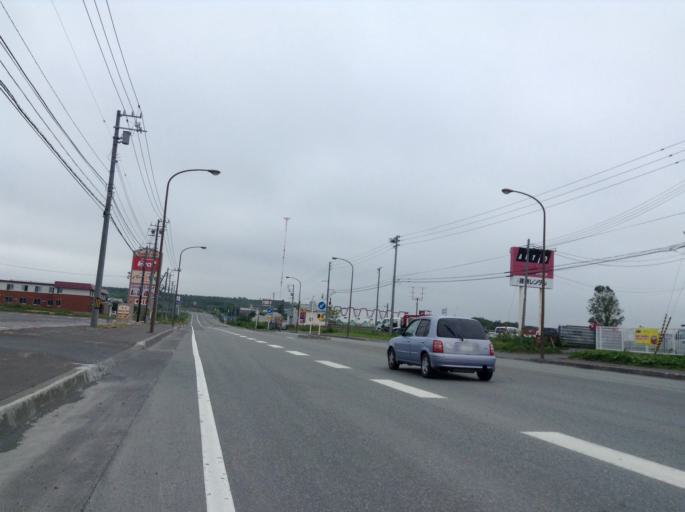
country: JP
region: Hokkaido
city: Wakkanai
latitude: 45.3808
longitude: 141.7095
